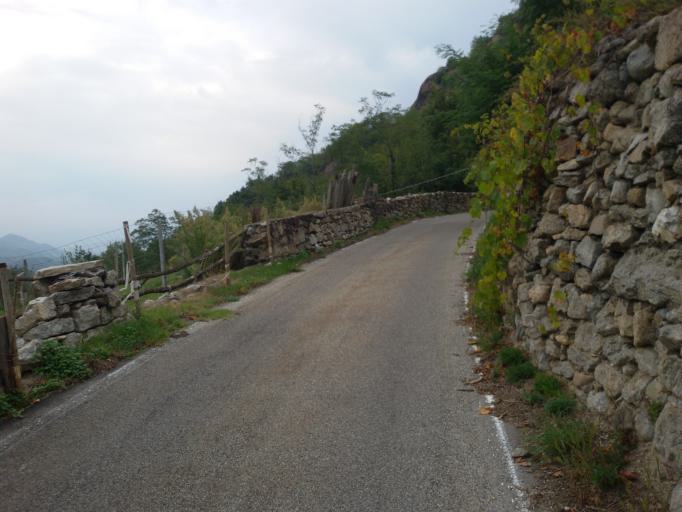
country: IT
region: Piedmont
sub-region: Provincia di Torino
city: Borgone Susa
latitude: 45.1259
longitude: 7.2362
